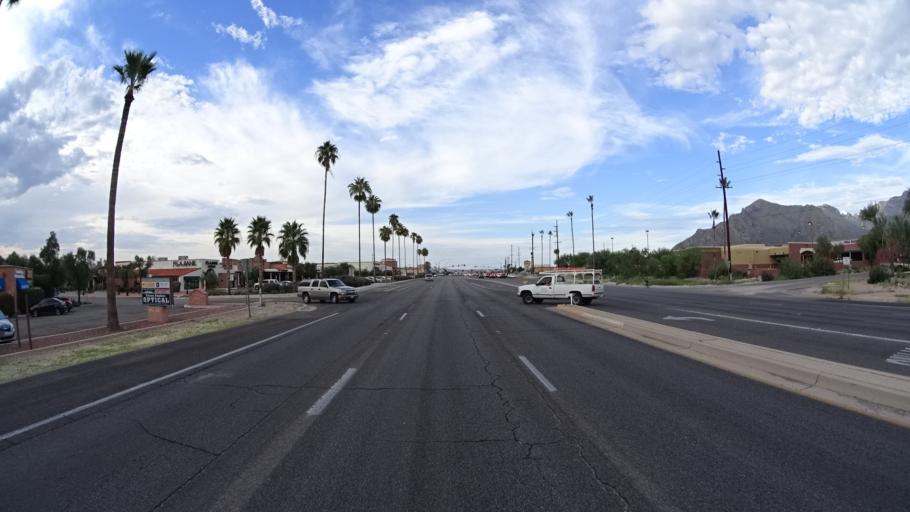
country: US
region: Arizona
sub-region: Pima County
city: Casas Adobes
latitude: 32.3344
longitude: -110.9774
